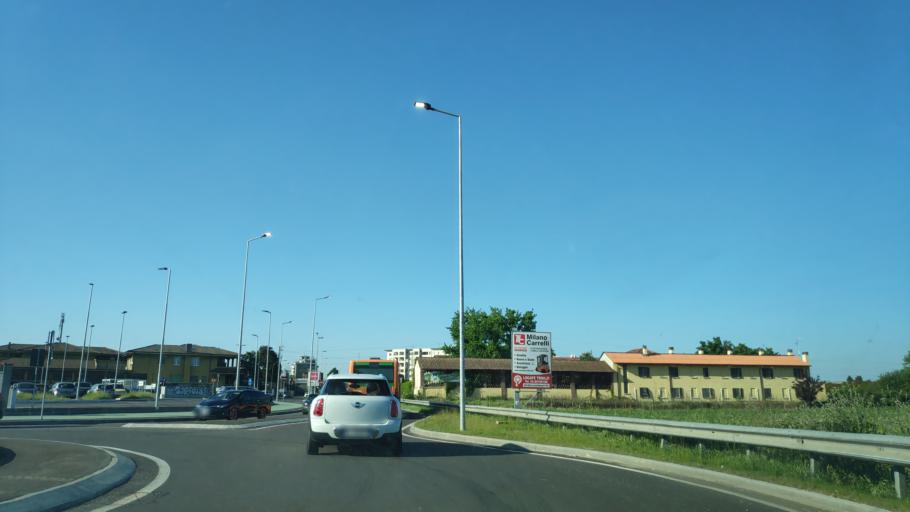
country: IT
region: Lombardy
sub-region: Citta metropolitana di Milano
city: Opera
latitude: 45.3672
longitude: 9.2093
